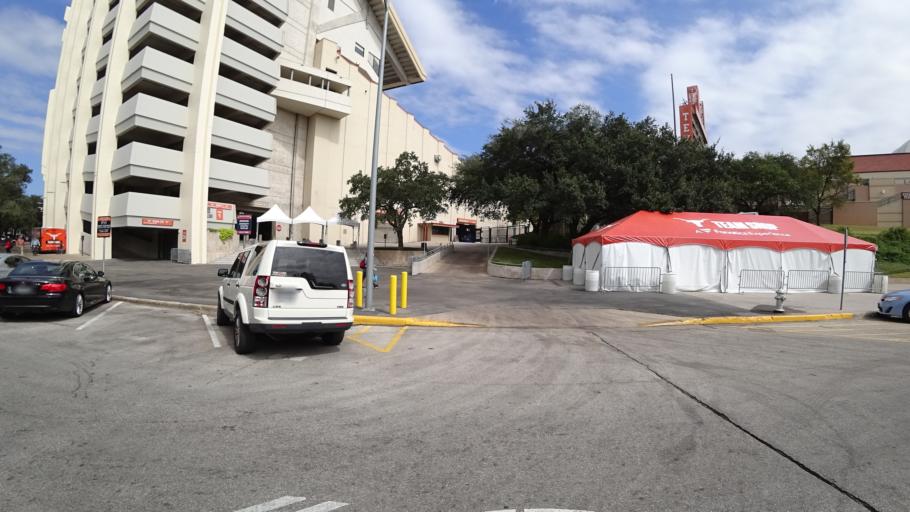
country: US
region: Texas
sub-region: Travis County
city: Austin
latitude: 30.2827
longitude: -97.7338
